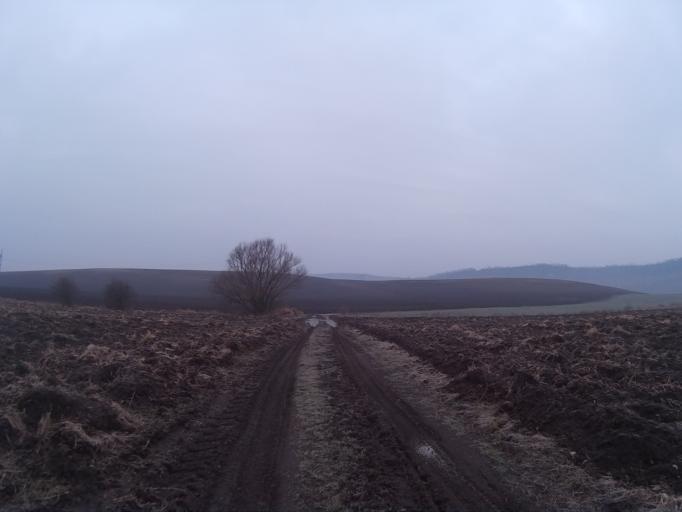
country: HU
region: Komarom-Esztergom
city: Tarjan
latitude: 47.6317
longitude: 18.5029
